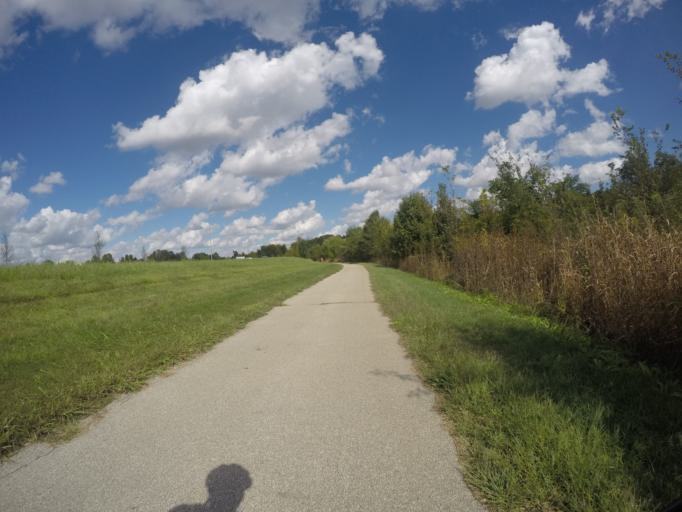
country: US
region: Kansas
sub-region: Johnson County
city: Lenexa
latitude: 38.9145
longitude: -94.7144
